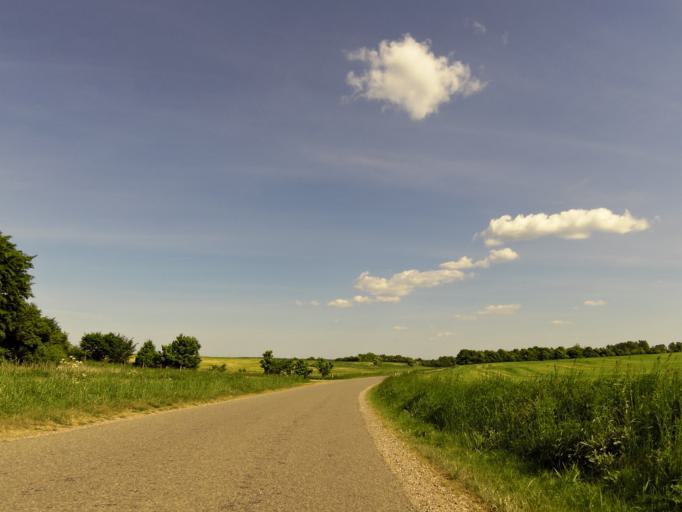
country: DK
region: Central Jutland
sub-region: Holstebro Kommune
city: Vinderup
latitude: 56.4364
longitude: 8.8772
